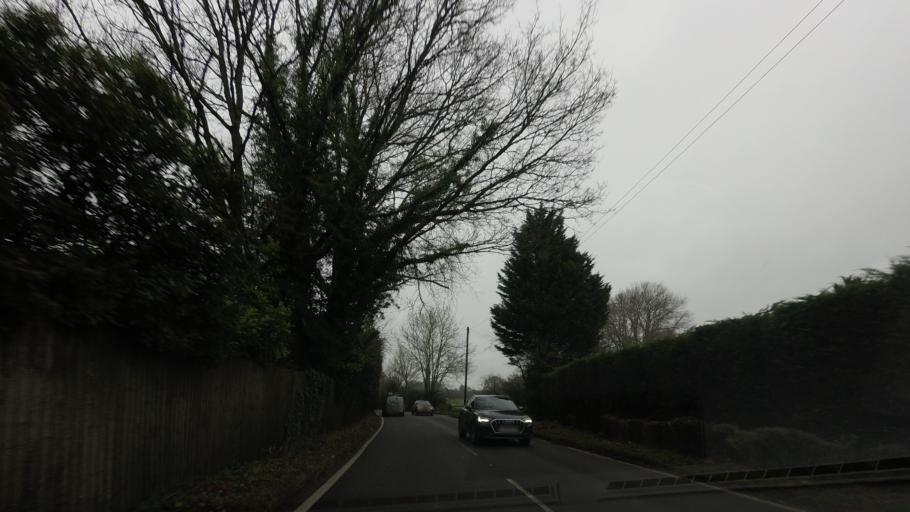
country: GB
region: England
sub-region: Kent
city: Hawkhurst
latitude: 51.0645
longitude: 0.5071
